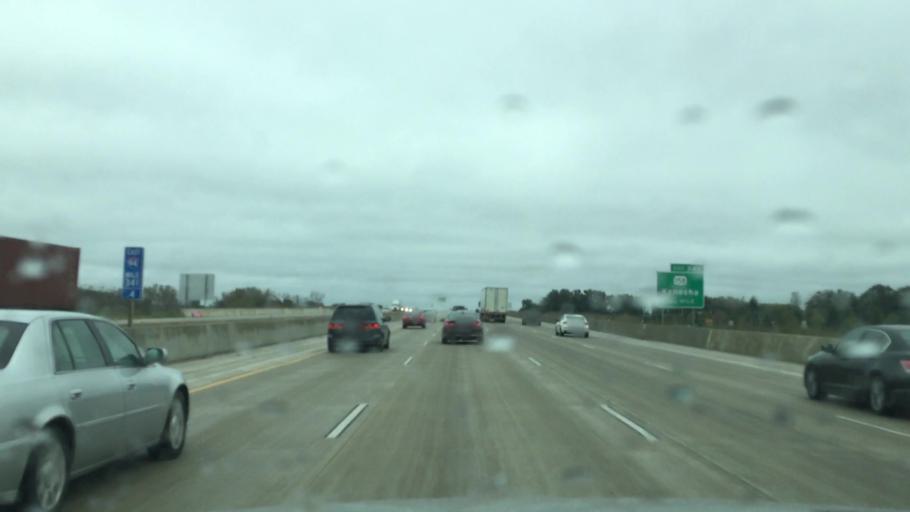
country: US
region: Wisconsin
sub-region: Kenosha County
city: Somers
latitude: 42.6078
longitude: -87.9523
